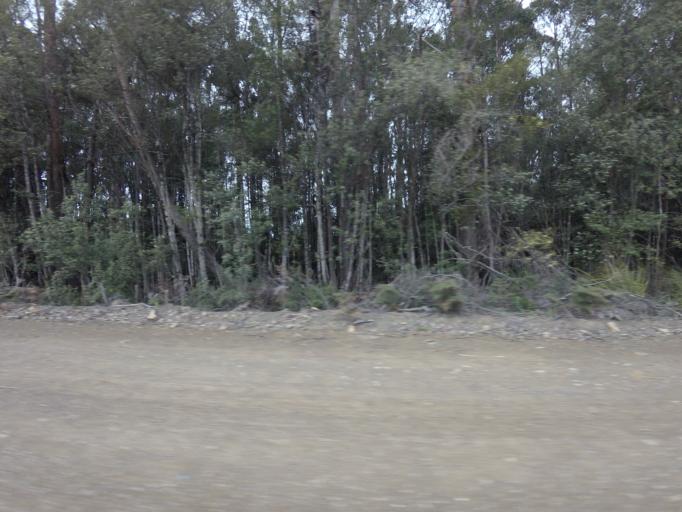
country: AU
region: Tasmania
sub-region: Huon Valley
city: Geeveston
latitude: -43.4886
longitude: 146.8893
